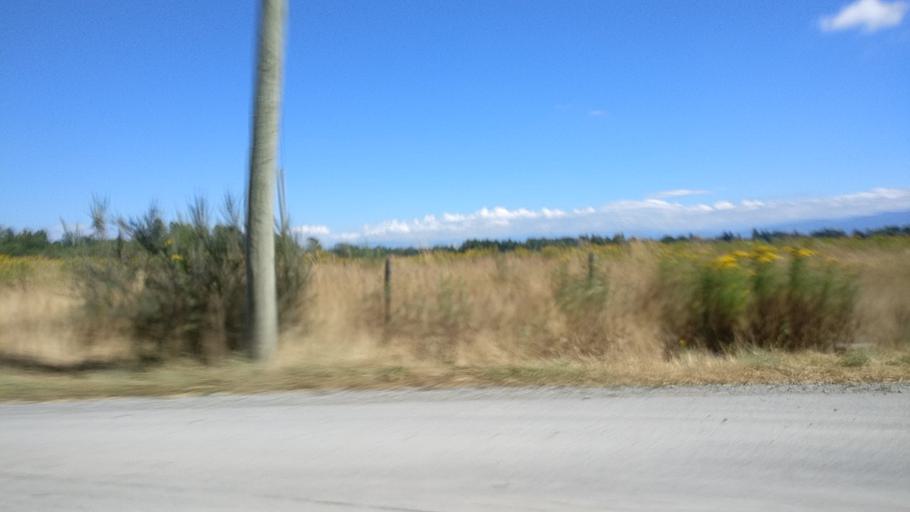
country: CA
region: British Columbia
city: Aldergrove
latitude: 49.0231
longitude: -122.4485
